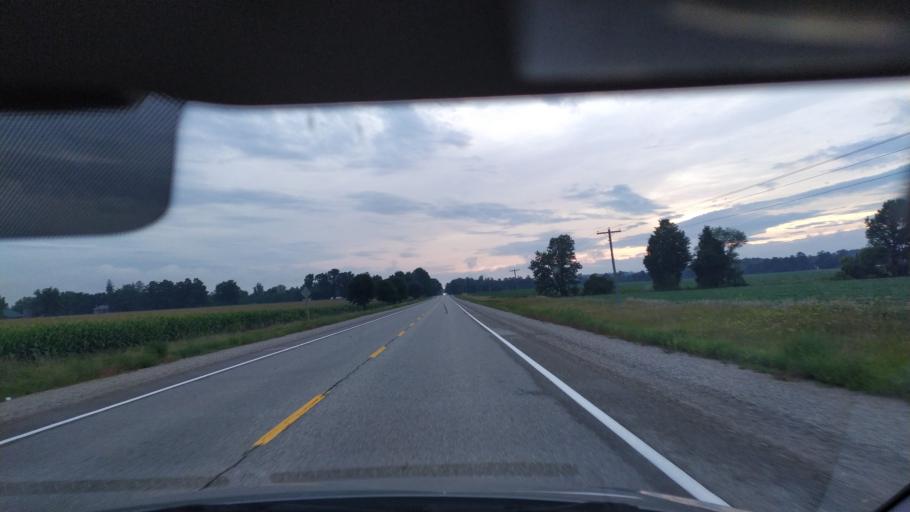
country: CA
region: Ontario
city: Kitchener
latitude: 43.3182
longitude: -80.5270
